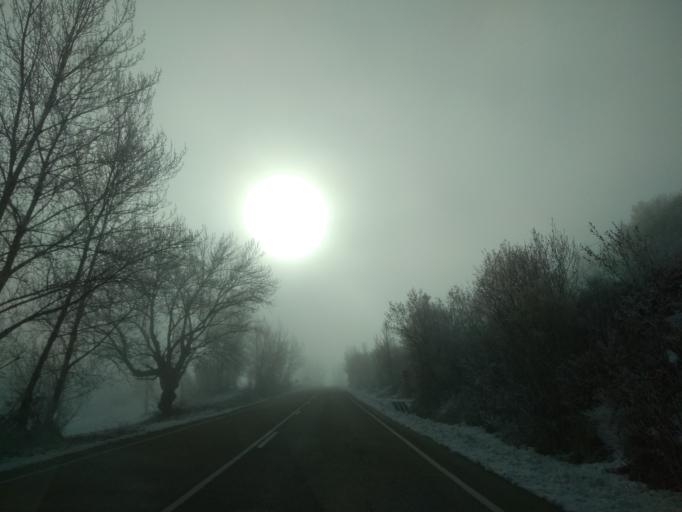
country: ES
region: Castille and Leon
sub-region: Provincia de Burgos
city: Medina de Pomar
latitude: 43.0015
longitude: -3.5187
